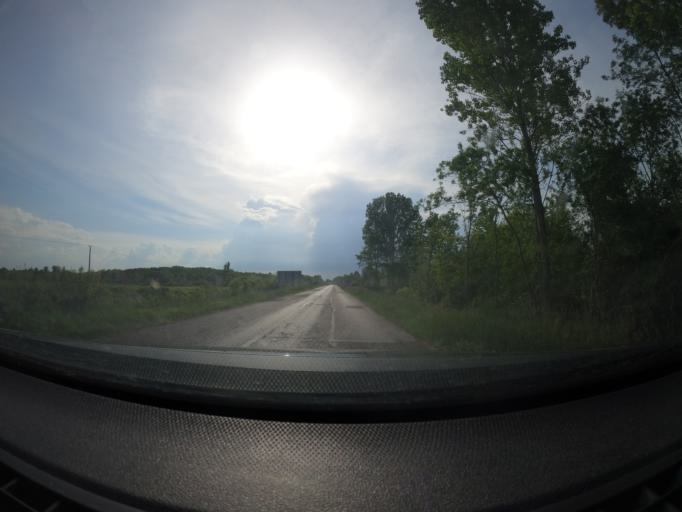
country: HU
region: Hajdu-Bihar
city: Nyirabrany
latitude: 47.5262
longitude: 21.9765
